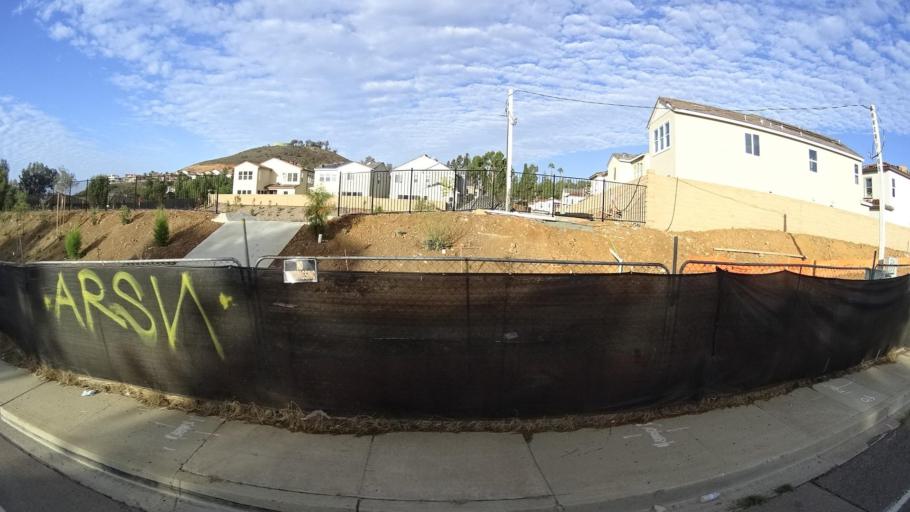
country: US
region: California
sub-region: San Diego County
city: Spring Valley
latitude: 32.7295
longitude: -116.9715
